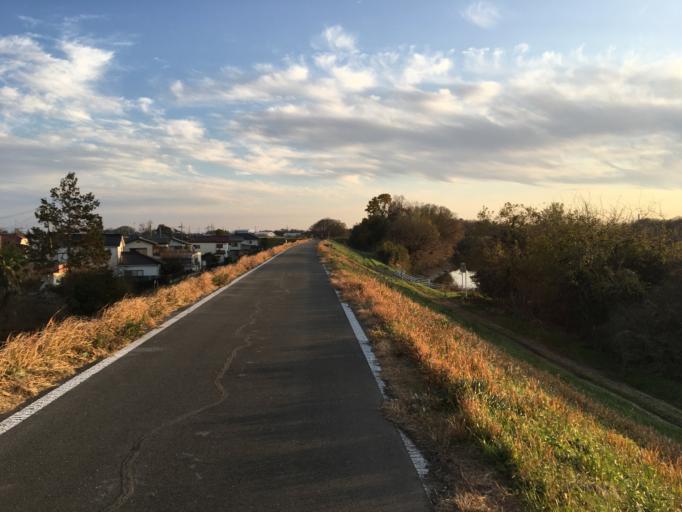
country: JP
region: Saitama
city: Kawagoe
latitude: 35.9674
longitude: 139.4635
